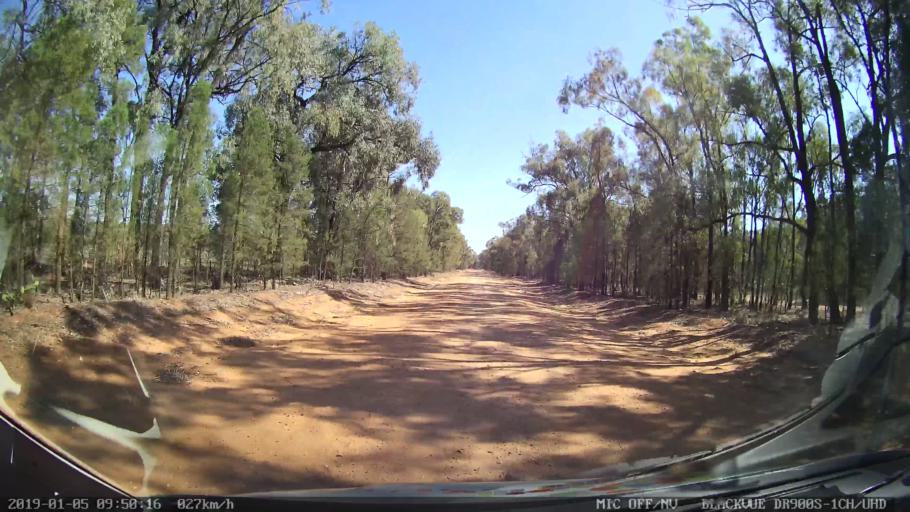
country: AU
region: New South Wales
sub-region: Gilgandra
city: Gilgandra
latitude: -31.6653
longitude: 148.7587
